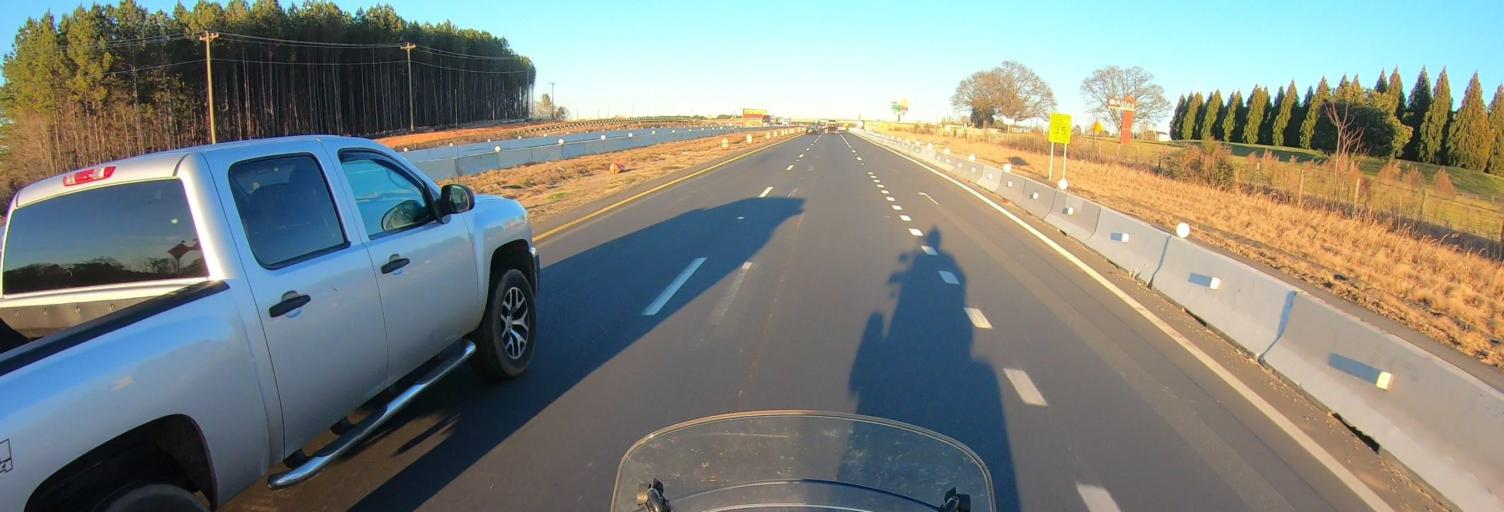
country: US
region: South Carolina
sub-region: Cherokee County
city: Blacksburg
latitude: 35.1547
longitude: -81.4833
